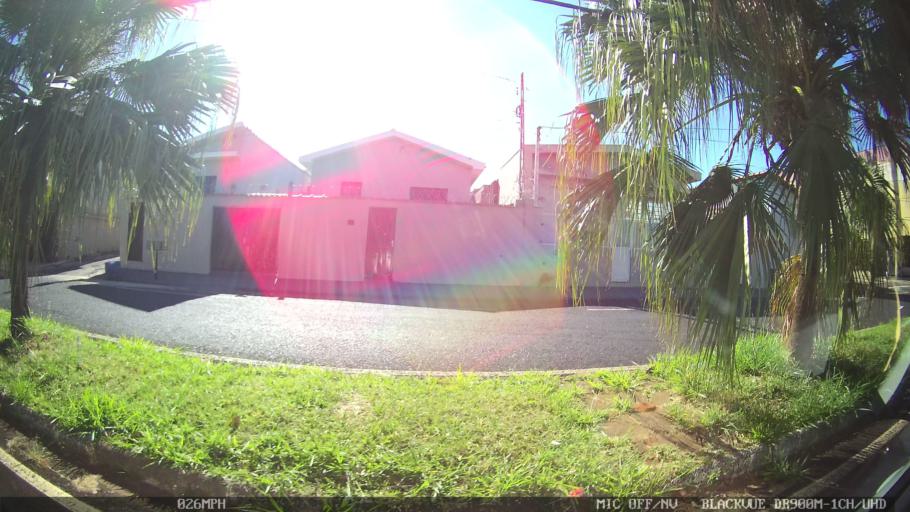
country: BR
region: Sao Paulo
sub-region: Franca
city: Franca
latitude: -20.5460
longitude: -47.3940
